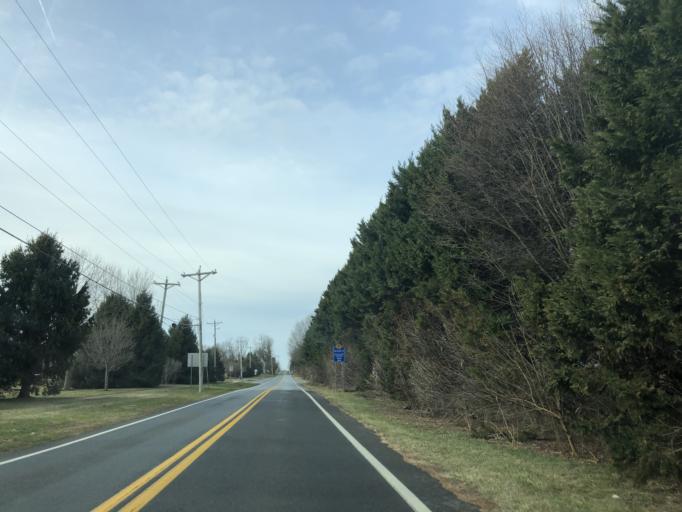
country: US
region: Delaware
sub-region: New Castle County
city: Townsend
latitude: 39.4454
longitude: -75.6314
